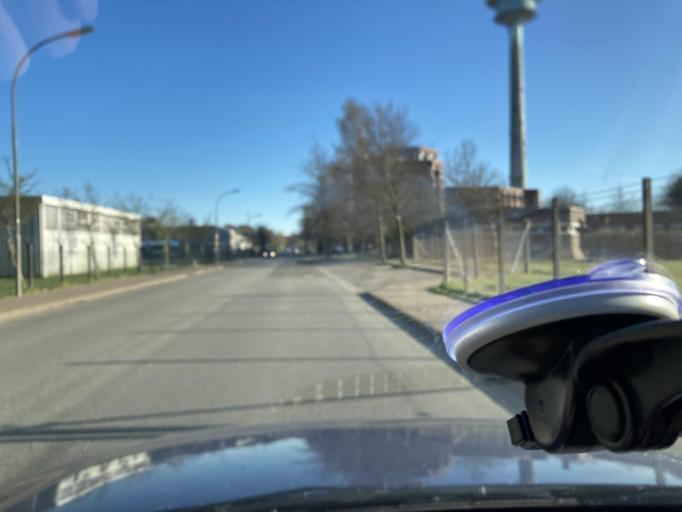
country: DE
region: Schleswig-Holstein
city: Heide
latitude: 54.2098
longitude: 9.0986
